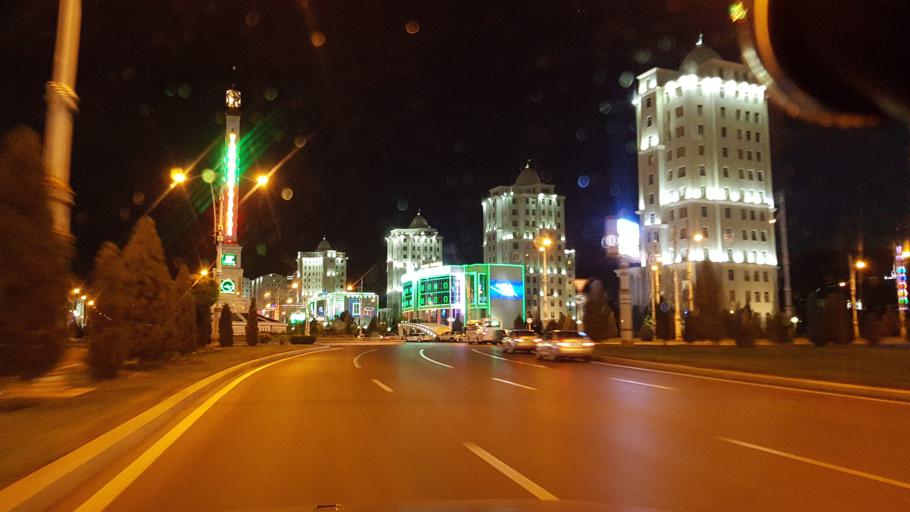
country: TM
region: Ahal
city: Ashgabat
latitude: 37.9059
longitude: 58.3363
